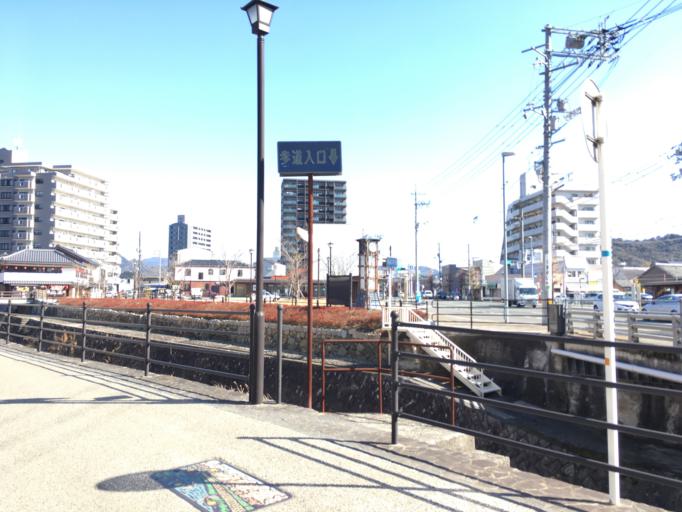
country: JP
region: Yamaguchi
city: Yamaguchi-shi
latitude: 34.1789
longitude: 131.4774
